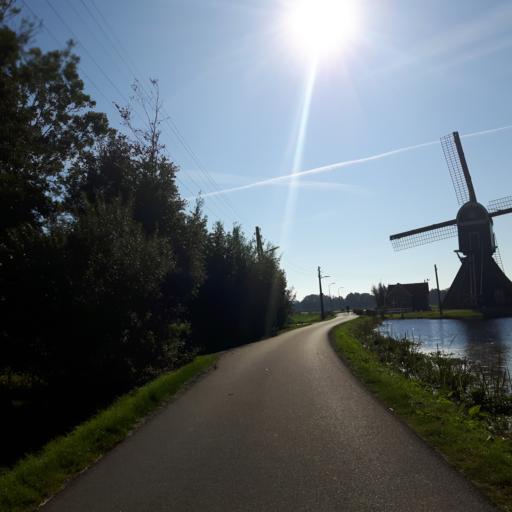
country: NL
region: South Holland
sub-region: Gemeente Schoonhoven
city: Schoonhoven
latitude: 51.9605
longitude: 4.8462
